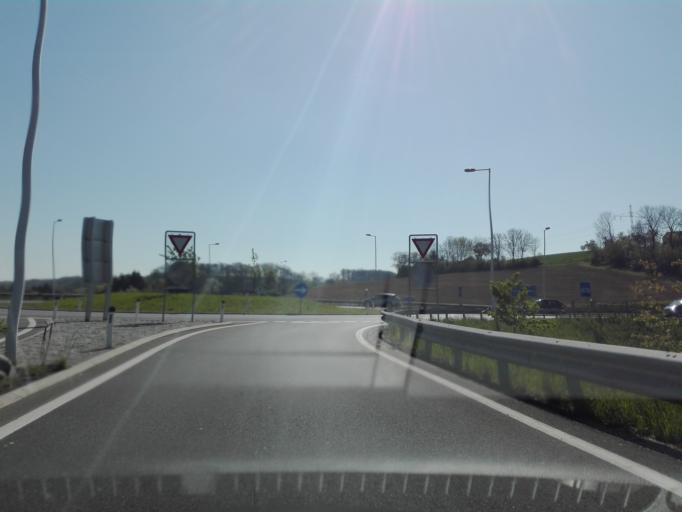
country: AT
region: Upper Austria
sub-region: Politischer Bezirk Linz-Land
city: Asten
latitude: 48.2073
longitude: 14.4341
